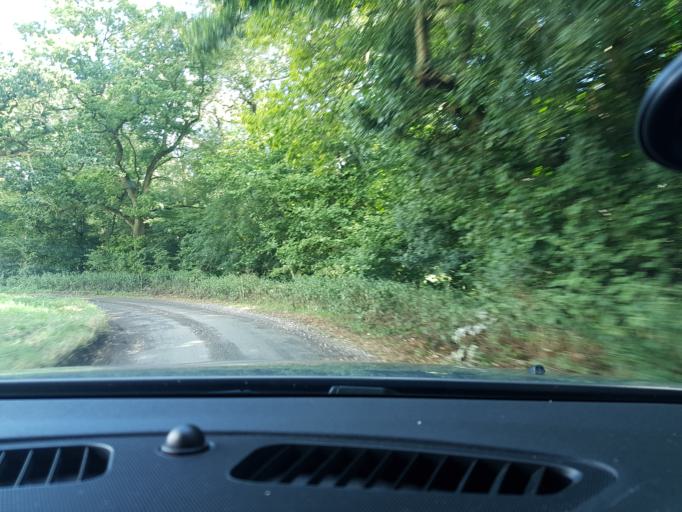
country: GB
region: England
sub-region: Wiltshire
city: Aldbourne
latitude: 51.4535
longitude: -1.6406
